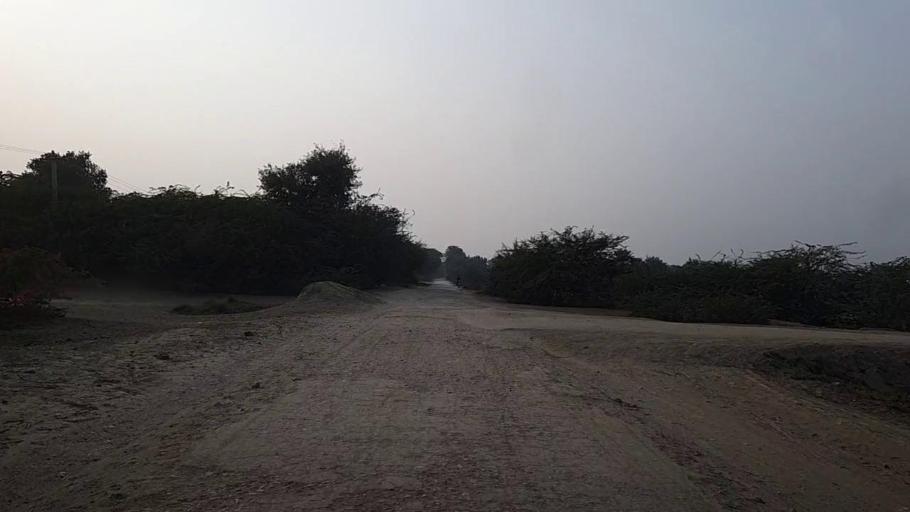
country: PK
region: Sindh
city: Setharja Old
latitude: 27.0811
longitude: 68.5243
